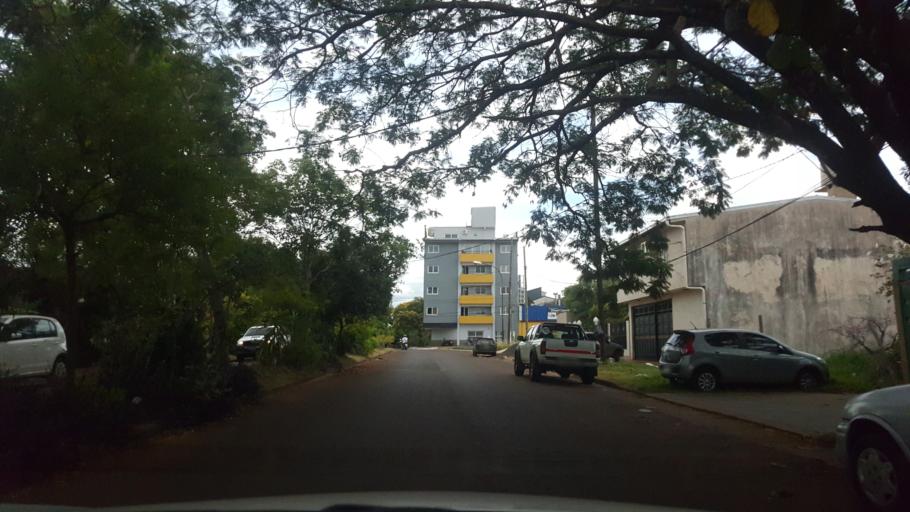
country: AR
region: Misiones
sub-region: Departamento de Capital
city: Posadas
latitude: -27.3995
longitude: -55.8935
